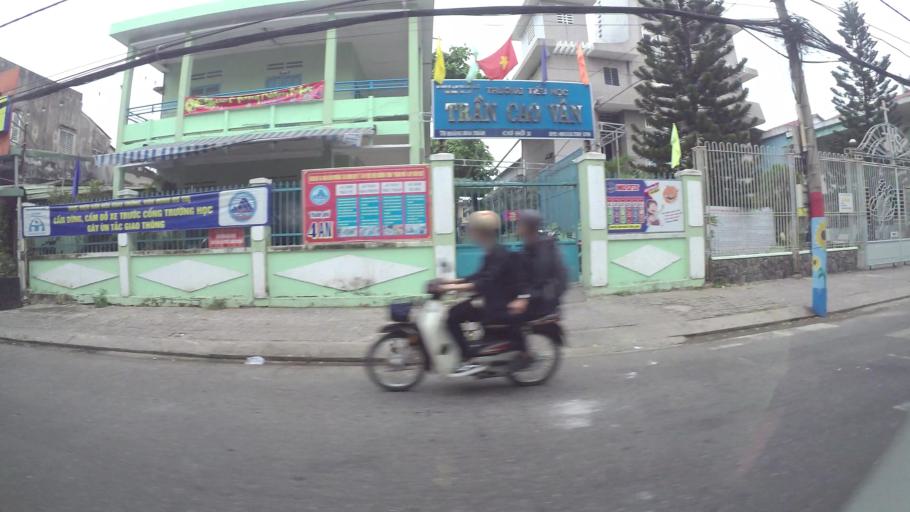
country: VN
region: Da Nang
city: Da Nang
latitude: 16.0683
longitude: 108.2099
